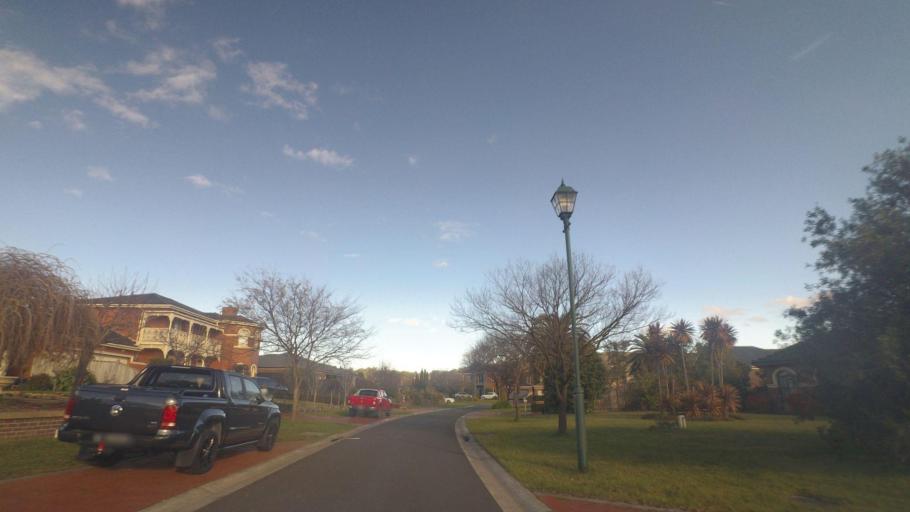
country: AU
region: Victoria
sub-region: Yarra Ranges
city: Lysterfield
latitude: -37.9159
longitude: 145.2853
